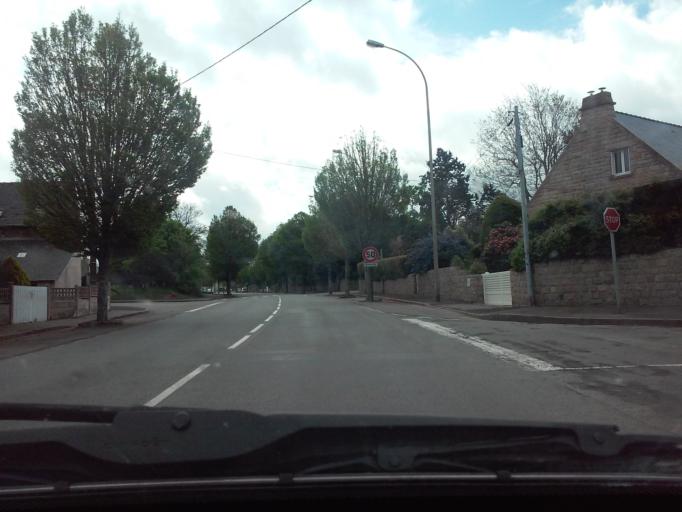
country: FR
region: Brittany
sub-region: Departement d'Ille-et-Vilaine
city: Dinard
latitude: 48.6296
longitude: -2.0755
